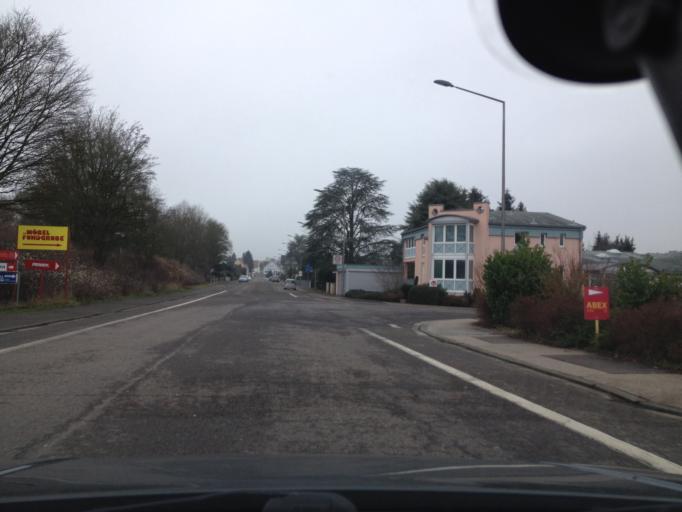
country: DE
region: Saarland
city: Homburg
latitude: 49.3283
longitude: 7.3198
